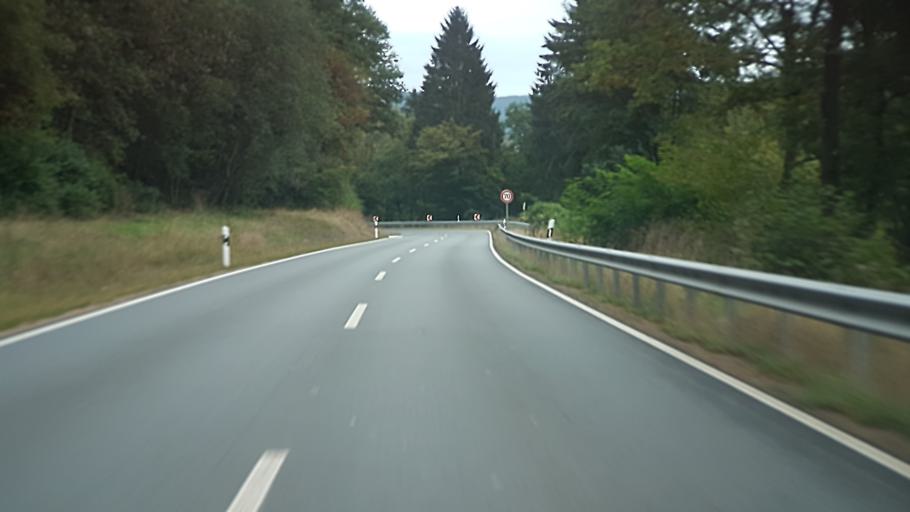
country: DE
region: North Rhine-Westphalia
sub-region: Regierungsbezirk Arnsberg
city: Attendorn
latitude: 51.1359
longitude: 7.8832
